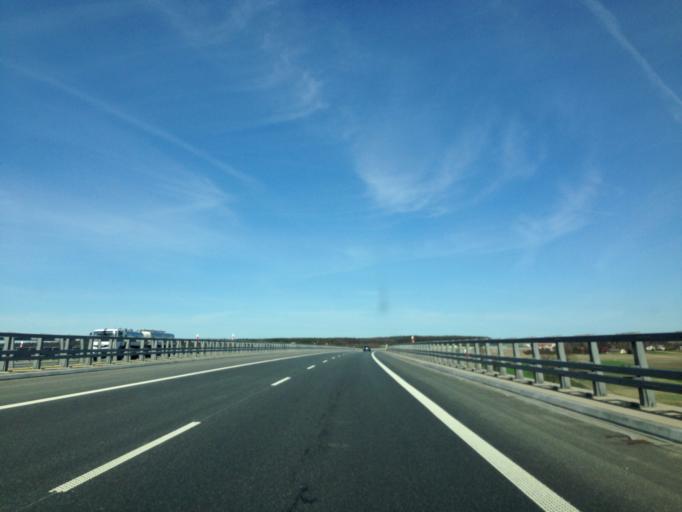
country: PL
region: Lodz Voivodeship
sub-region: Powiat sieradzki
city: Sieradz
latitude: 51.5841
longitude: 18.8027
